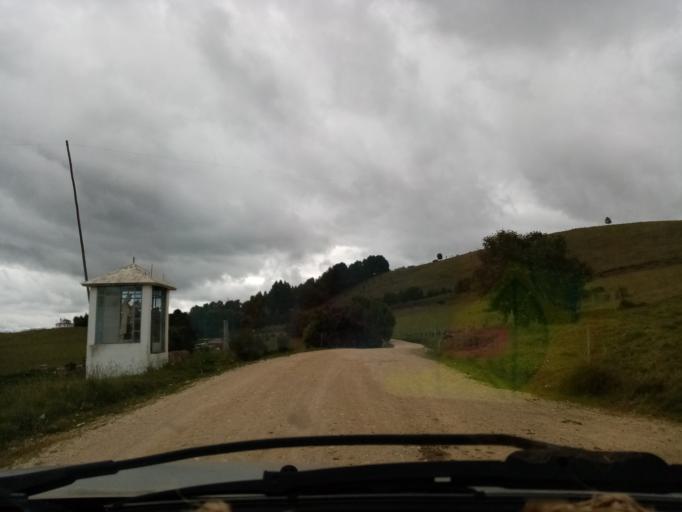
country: CO
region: Boyaca
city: Toca
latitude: 5.6051
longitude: -73.2378
